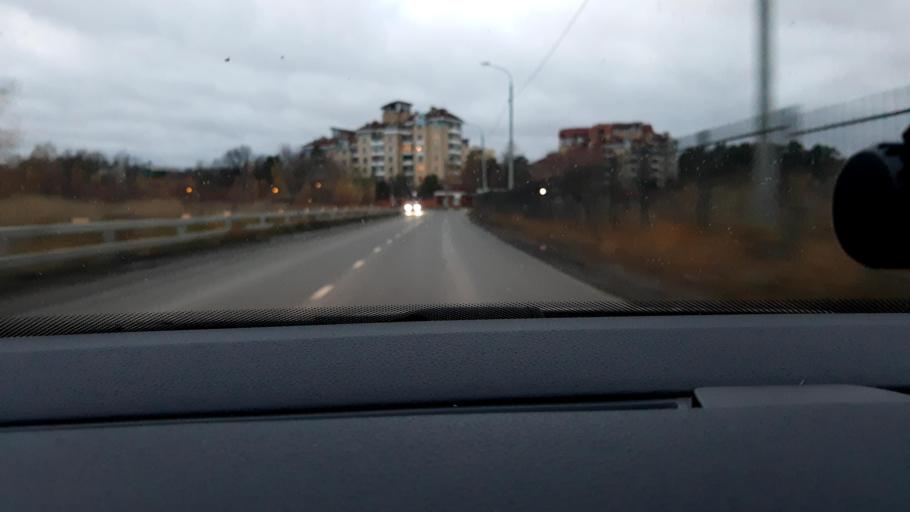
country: RU
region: Moskovskaya
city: Zarech'ye
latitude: 55.6793
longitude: 37.3925
